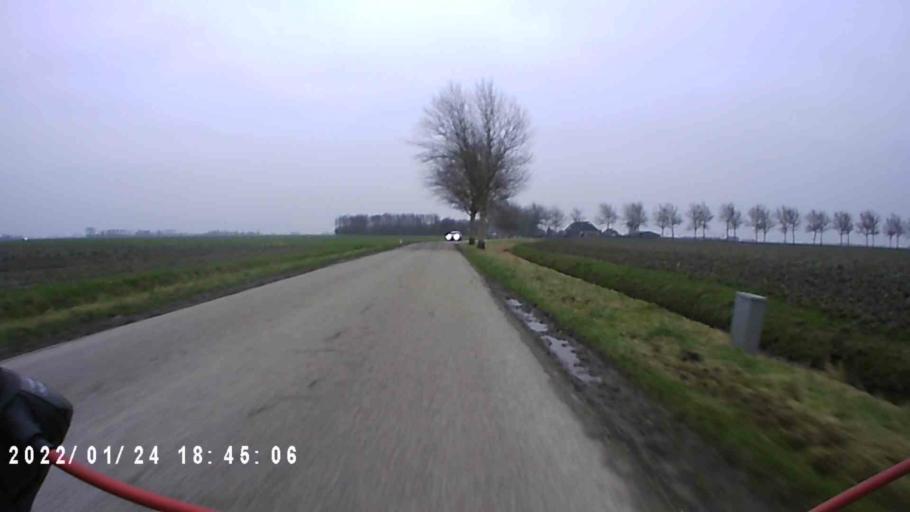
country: NL
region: Groningen
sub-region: Gemeente De Marne
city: Ulrum
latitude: 53.3400
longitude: 6.3690
